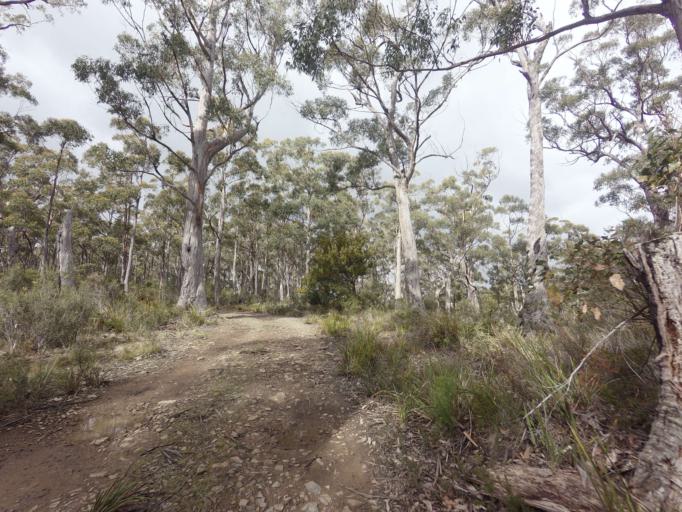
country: AU
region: Tasmania
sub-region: Huon Valley
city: Geeveston
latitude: -43.4609
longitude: 146.9092
